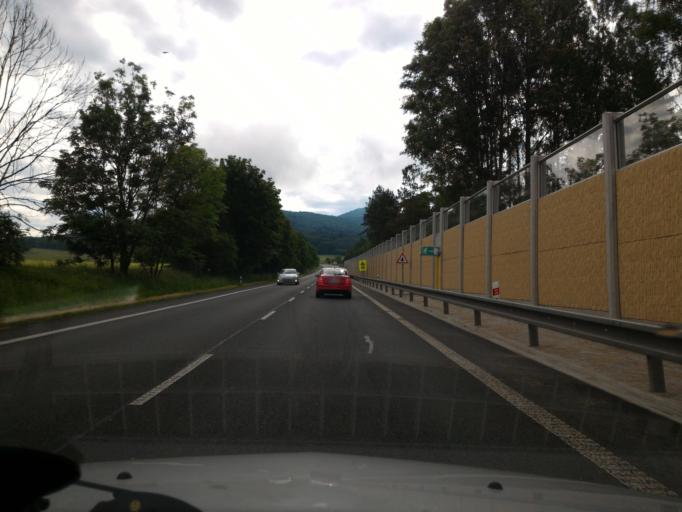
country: CZ
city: Hradek nad Nisou
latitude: 50.7952
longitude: 14.8480
